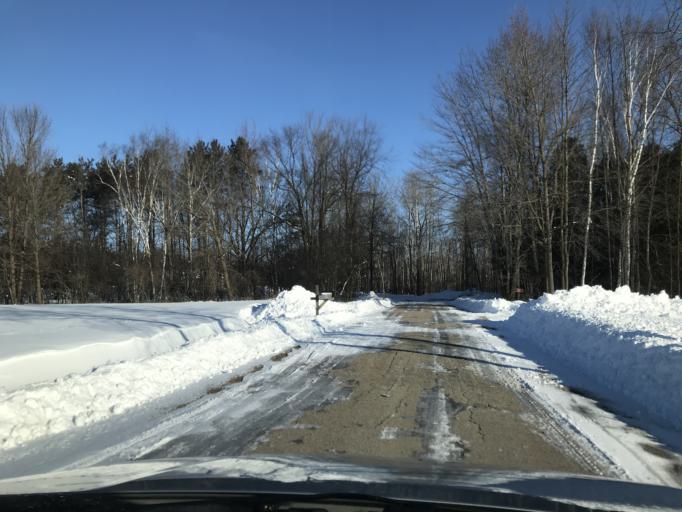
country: US
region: Wisconsin
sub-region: Oconto County
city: Oconto
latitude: 44.9567
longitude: -87.9768
